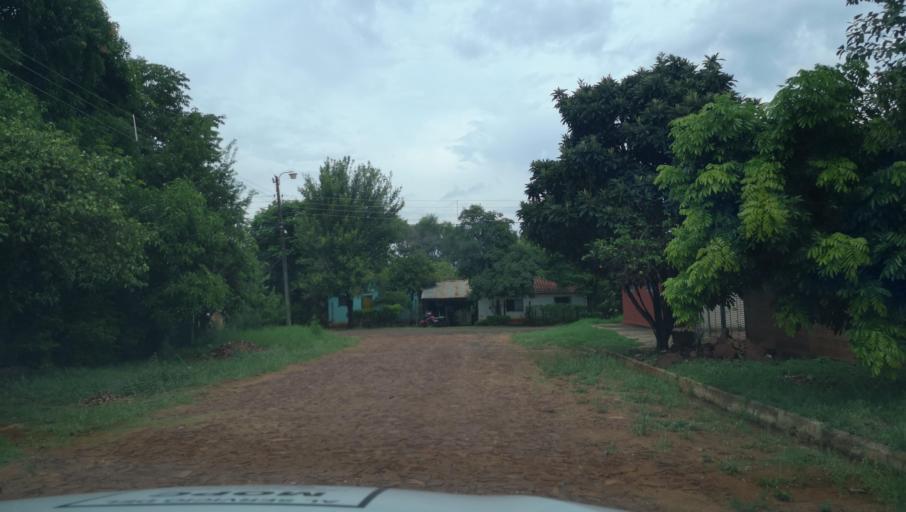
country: PY
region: Misiones
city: Santa Maria
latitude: -26.8895
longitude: -57.0437
